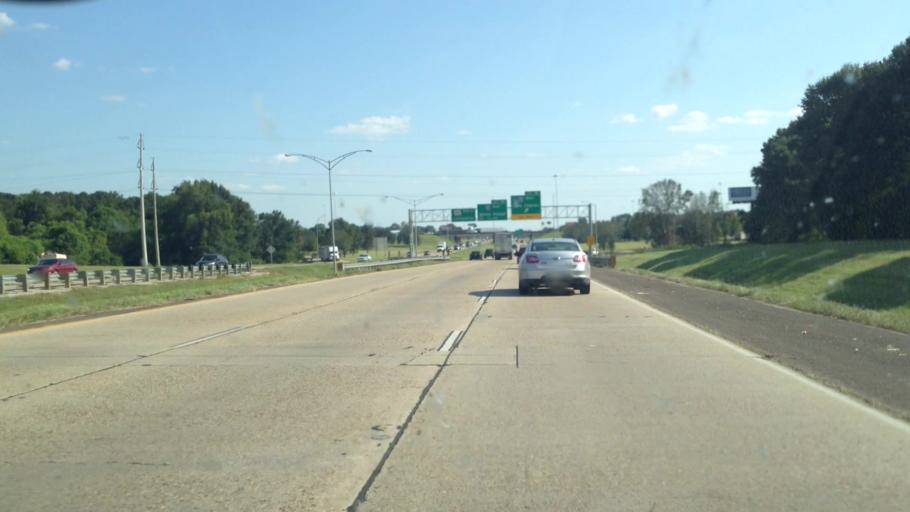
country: US
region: Louisiana
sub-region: Lafayette Parish
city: Lafayette
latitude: 30.2656
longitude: -92.0172
